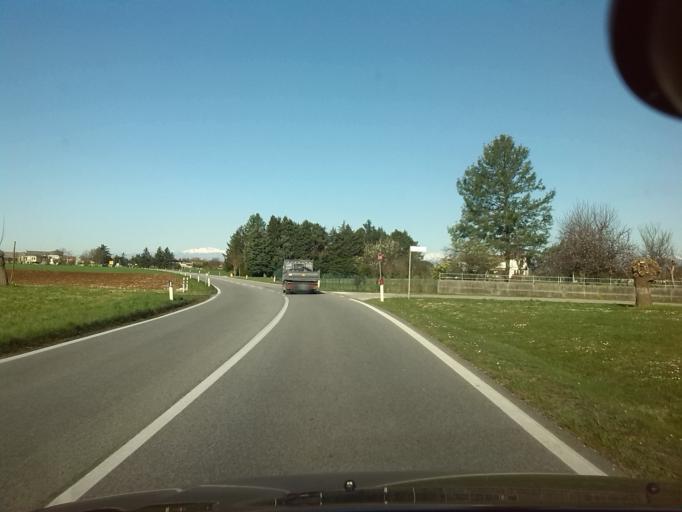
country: IT
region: Friuli Venezia Giulia
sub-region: Provincia di Udine
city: Moimacco
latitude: 46.0857
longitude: 13.3771
